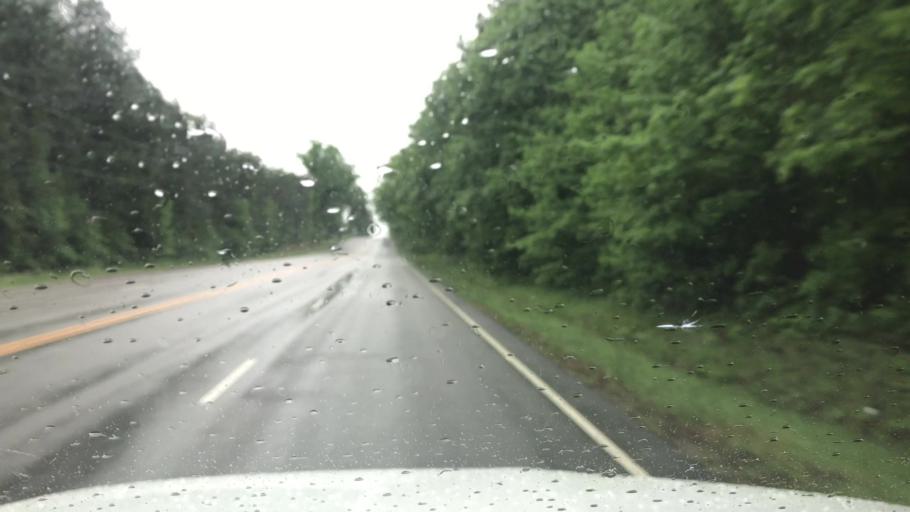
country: US
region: Virginia
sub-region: Hanover County
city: Ashland
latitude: 37.8388
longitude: -77.4671
